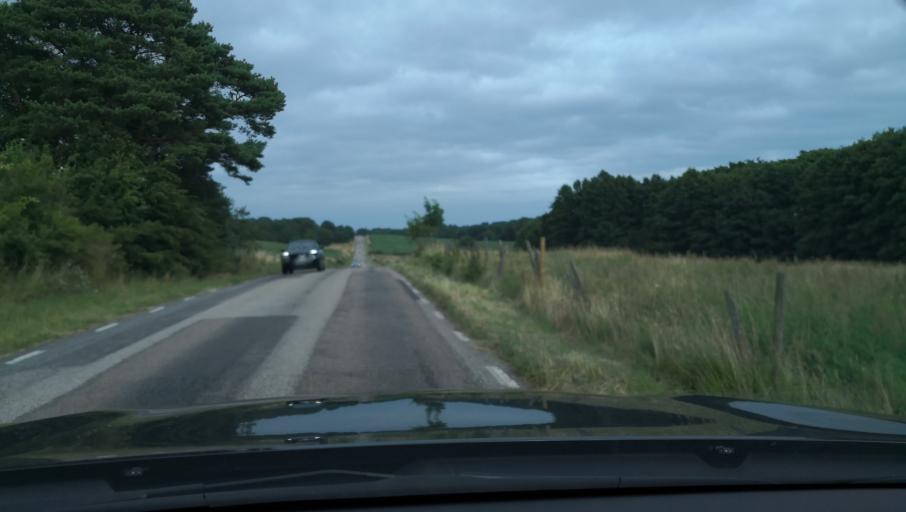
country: SE
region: Skane
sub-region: Simrishamns Kommun
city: Kivik
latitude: 55.6968
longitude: 14.1765
